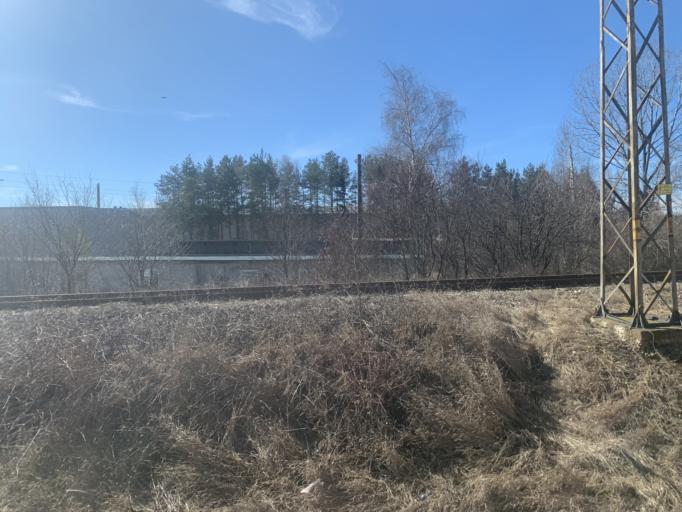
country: BG
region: Sofiya
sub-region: Obshtina Gorna Malina
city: Gorna Malina
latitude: 42.5583
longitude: 23.7024
